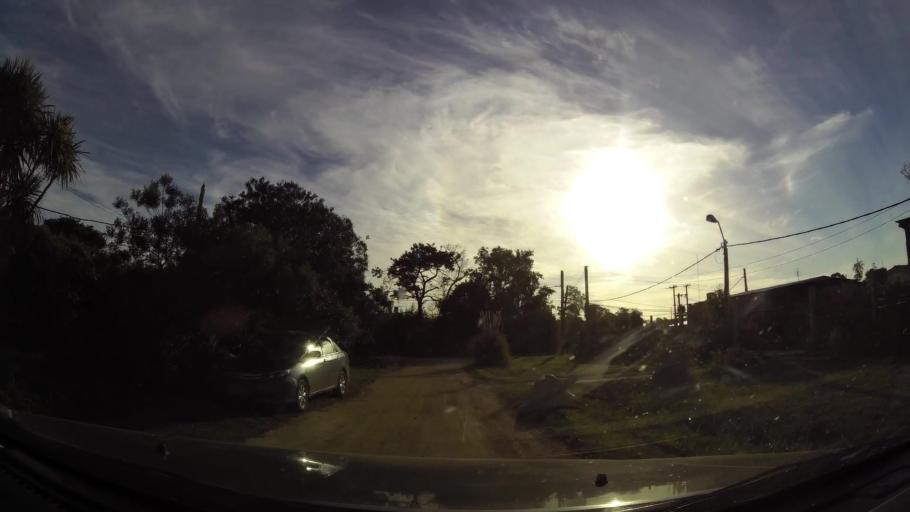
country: UY
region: Canelones
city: Empalme Olmos
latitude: -34.7780
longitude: -55.8649
